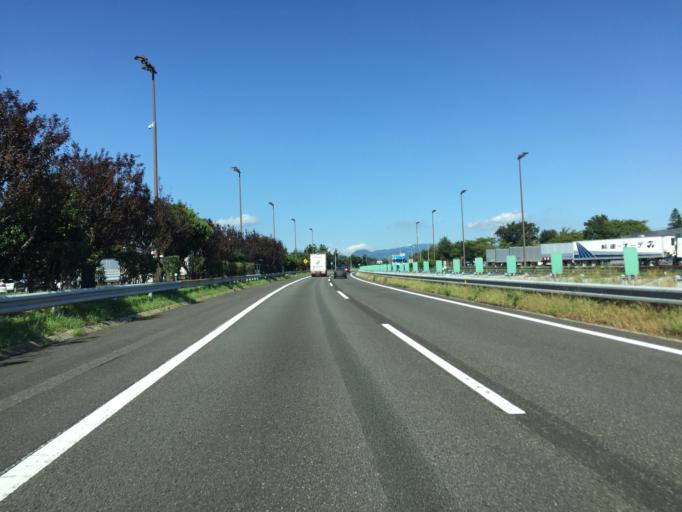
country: JP
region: Fukushima
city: Fukushima-shi
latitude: 37.7589
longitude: 140.4082
